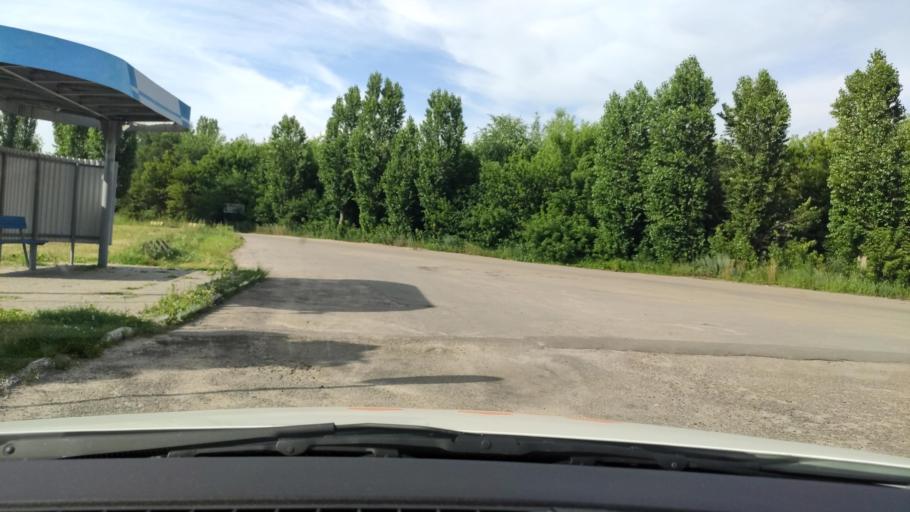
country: RU
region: Voronezj
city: Novaya Usman'
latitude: 51.6392
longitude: 39.3080
